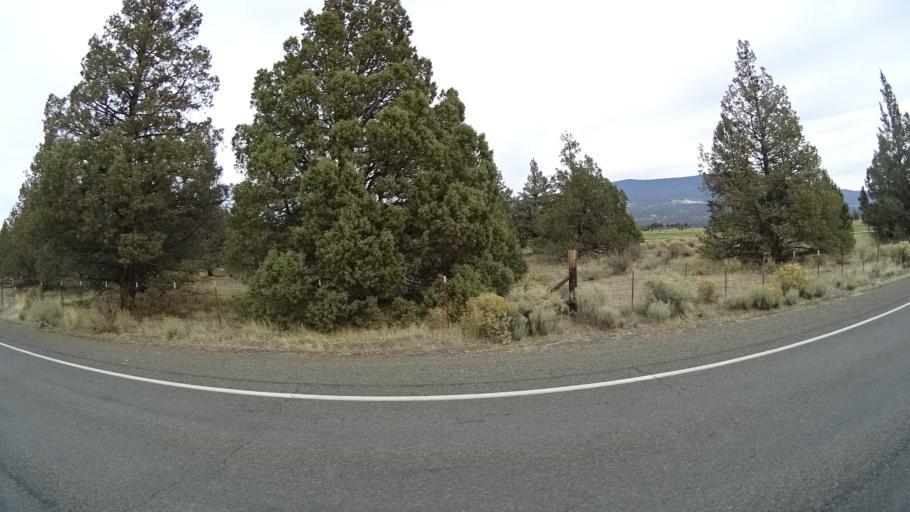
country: US
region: California
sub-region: Siskiyou County
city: Weed
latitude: 41.5995
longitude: -122.3462
